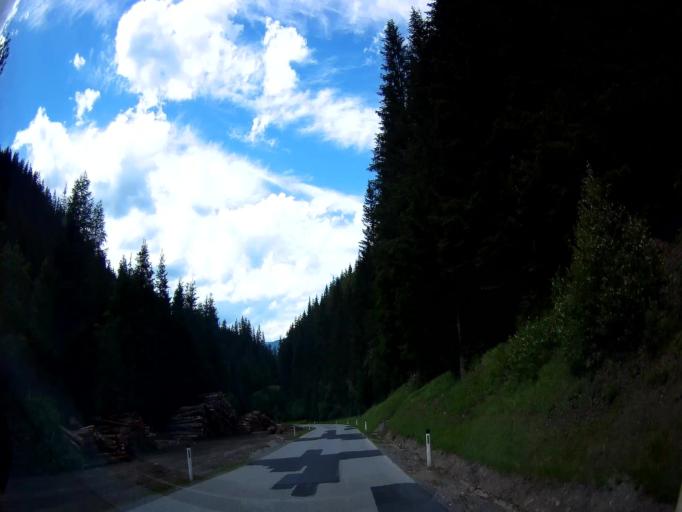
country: AT
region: Styria
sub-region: Politischer Bezirk Murau
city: Stadl an der Mur
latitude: 47.0330
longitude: 14.0057
